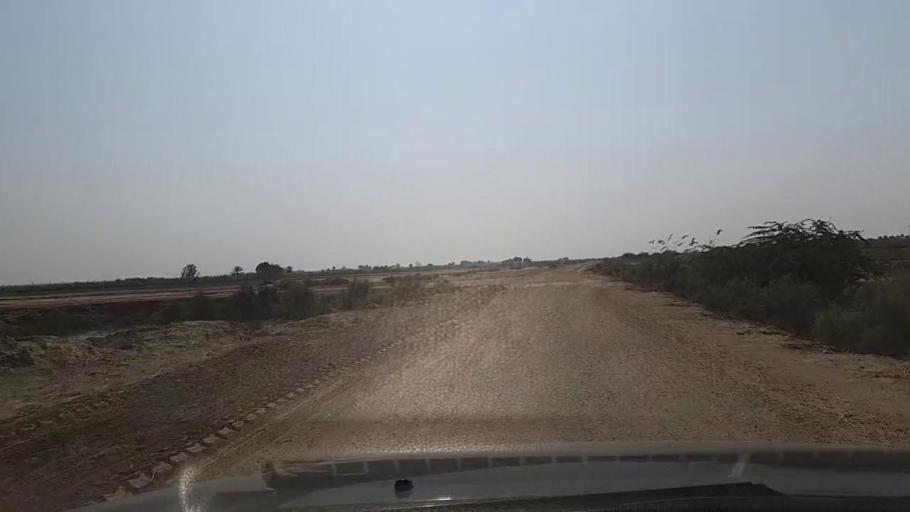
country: PK
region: Sindh
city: Mirpur Sakro
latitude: 24.3889
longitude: 67.6650
